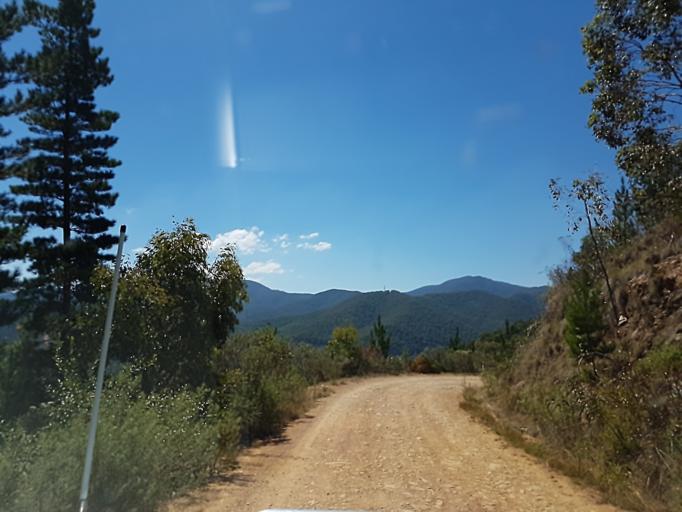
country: AU
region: Victoria
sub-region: Alpine
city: Mount Beauty
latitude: -36.7433
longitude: 146.9591
